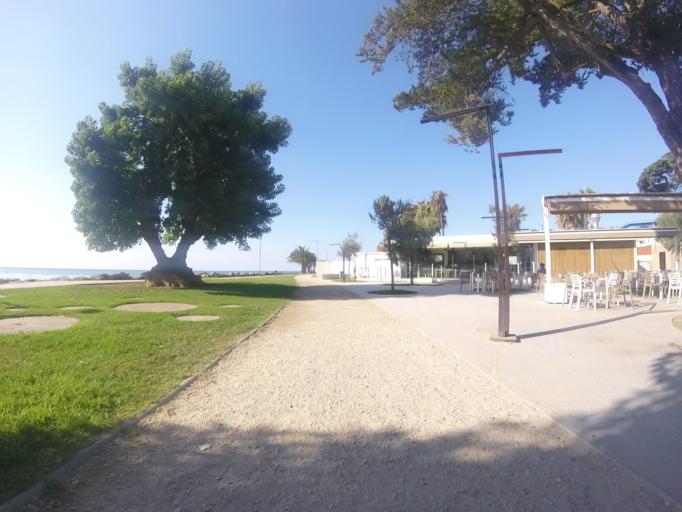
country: ES
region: Valencia
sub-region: Provincia de Castello
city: Benicarlo
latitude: 40.4118
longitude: 0.4298
